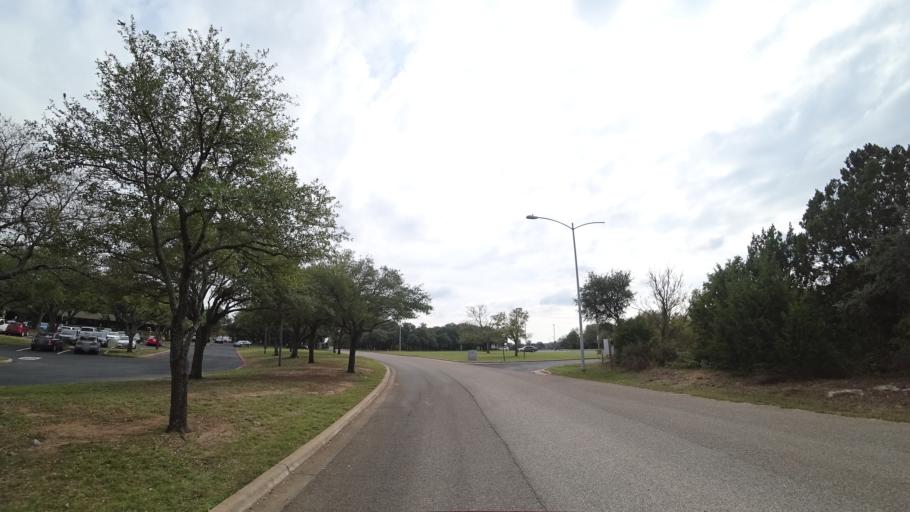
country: US
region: Texas
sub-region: Travis County
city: Wells Branch
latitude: 30.4473
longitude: -97.6933
